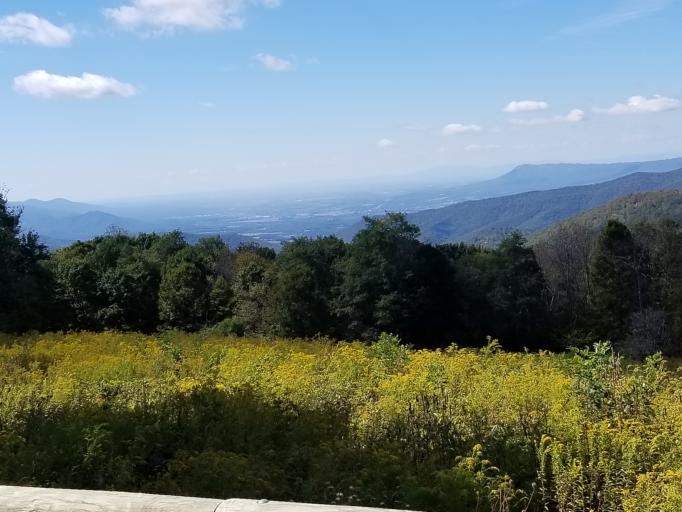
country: US
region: Virginia
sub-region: Page County
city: Stanley
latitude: 38.4938
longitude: -78.4508
